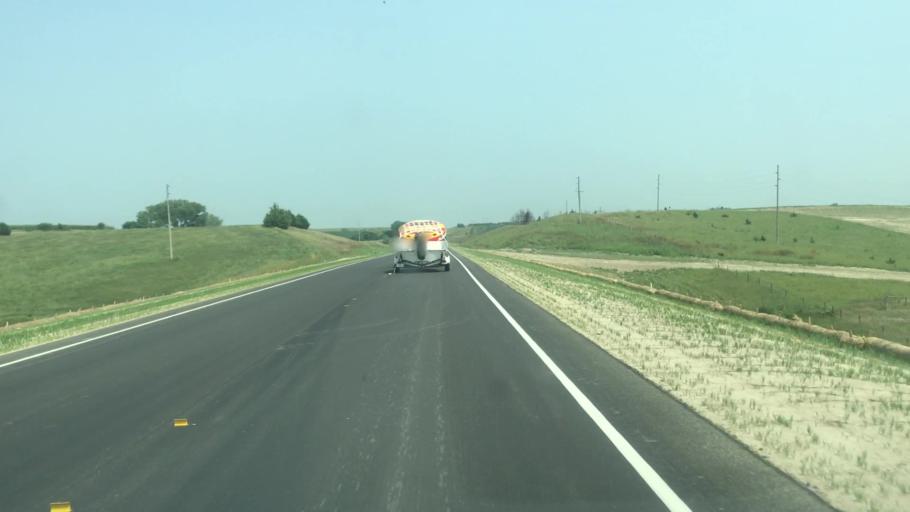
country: US
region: Nebraska
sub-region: Sherman County
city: Loup City
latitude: 41.2635
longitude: -98.9233
